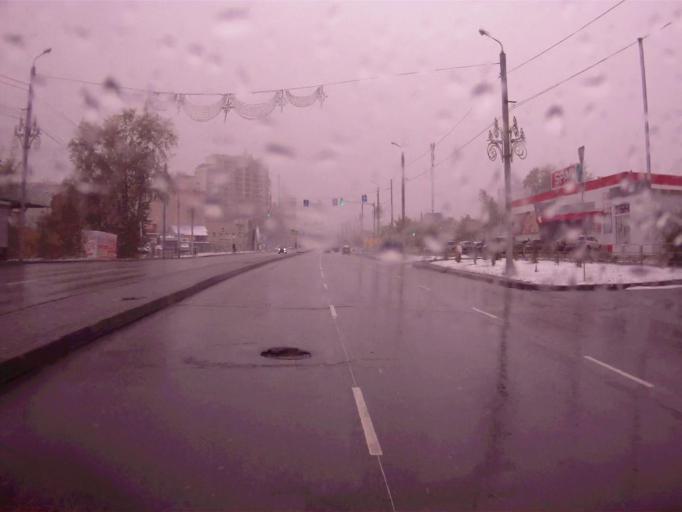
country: RU
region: Chelyabinsk
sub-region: Gorod Chelyabinsk
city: Chelyabinsk
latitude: 55.1439
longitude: 61.4057
